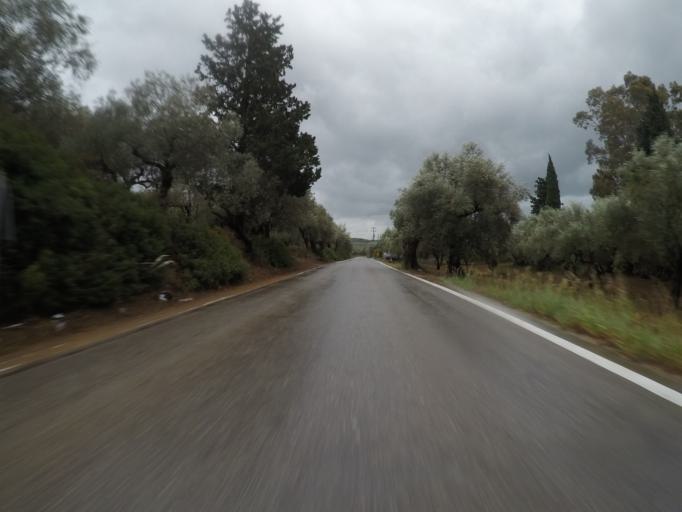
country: GR
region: Peloponnese
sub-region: Nomos Messinias
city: Pylos
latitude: 36.9852
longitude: 21.6818
